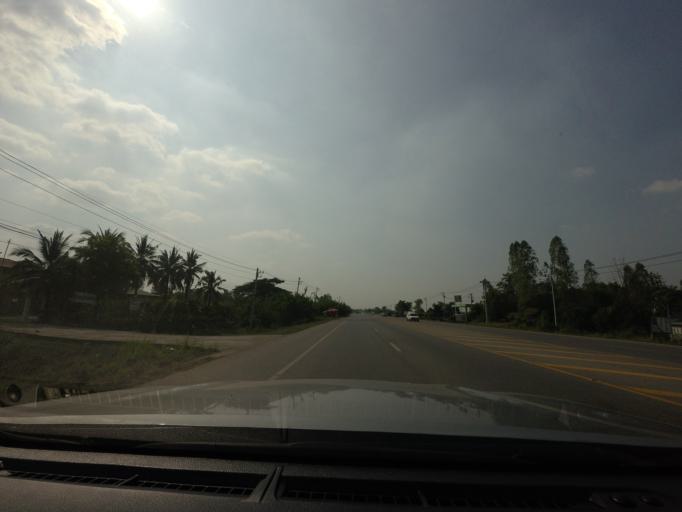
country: TH
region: Phitsanulok
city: Bang Rakam
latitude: 16.7650
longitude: 100.1328
